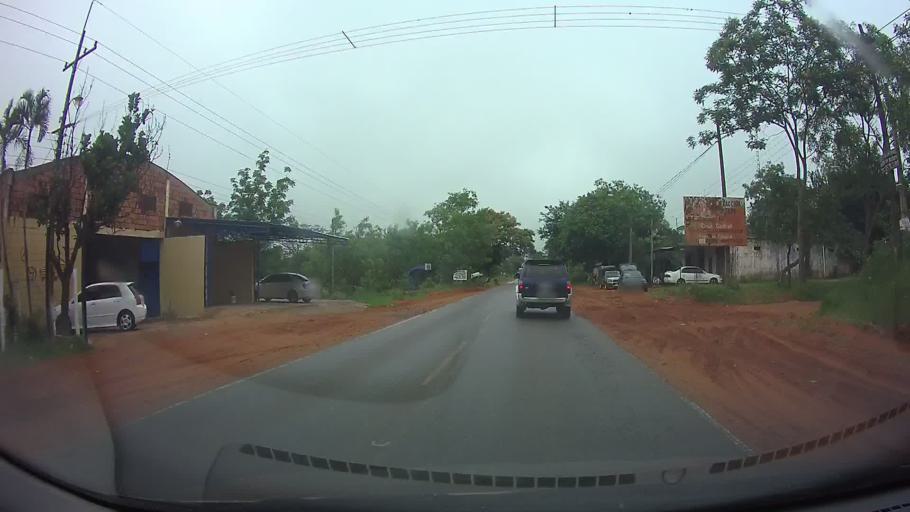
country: PY
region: Central
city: Ita
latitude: -25.4444
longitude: -57.3687
